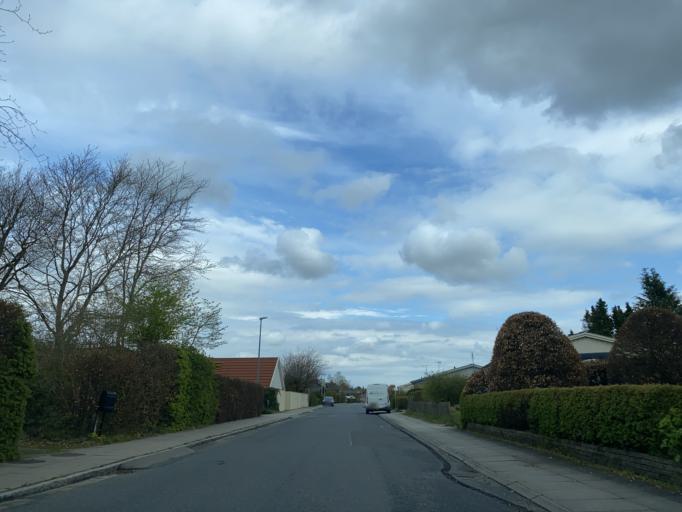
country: DK
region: Central Jutland
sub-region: Silkeborg Kommune
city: Svejbaek
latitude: 56.1735
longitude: 9.6168
